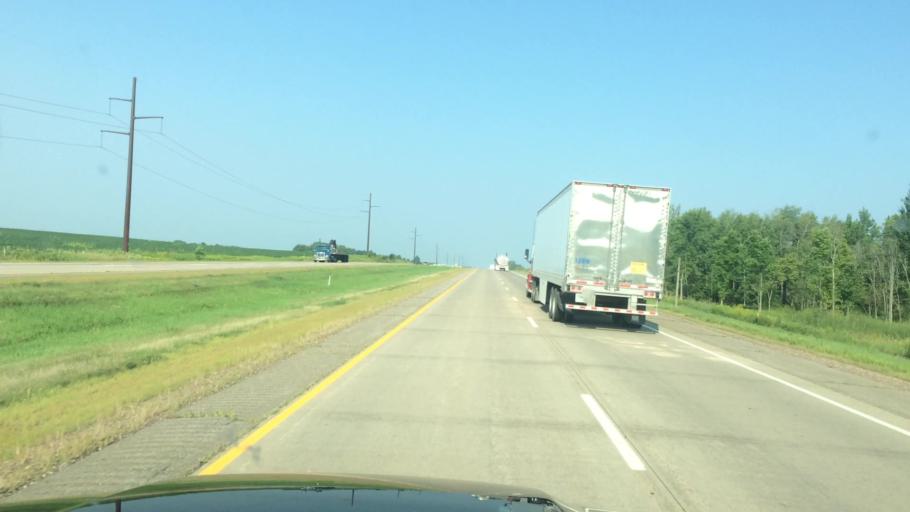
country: US
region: Wisconsin
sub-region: Marathon County
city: Edgar
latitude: 44.9445
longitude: -89.9836
